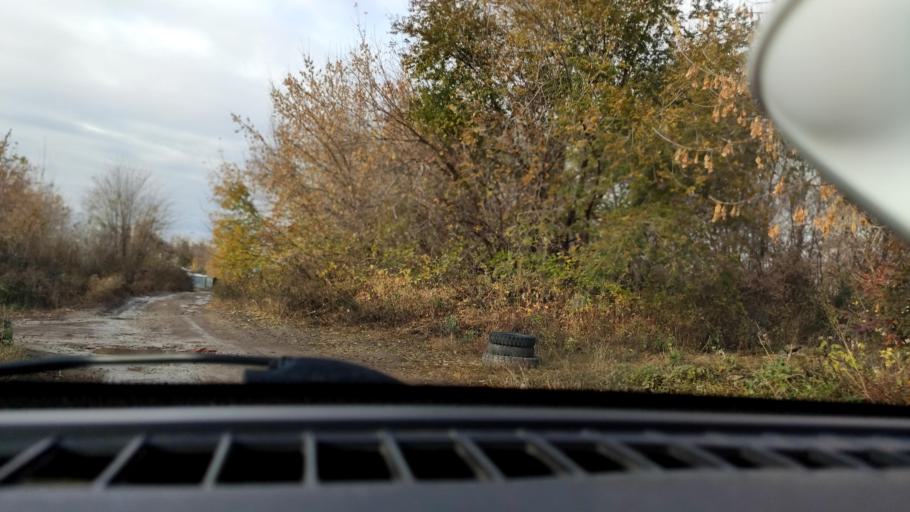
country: RU
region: Samara
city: Samara
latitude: 53.2043
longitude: 50.1995
